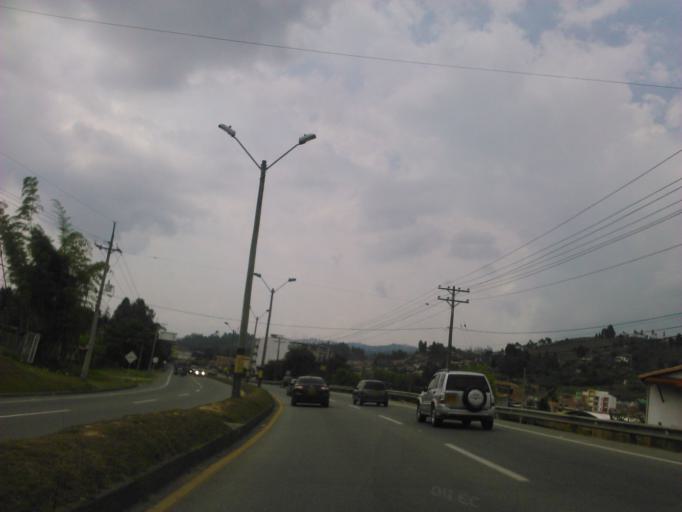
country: CO
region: Antioquia
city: Guarne
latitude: 6.2689
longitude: -75.4375
